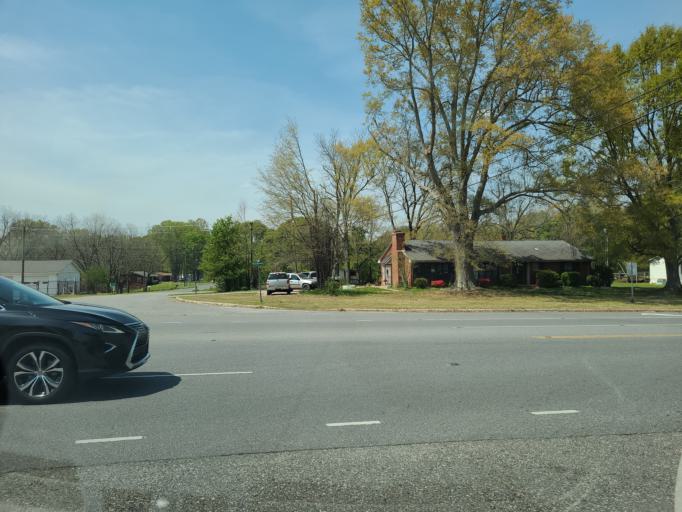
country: US
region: North Carolina
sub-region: Cleveland County
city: Shelby
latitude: 35.2639
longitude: -81.4984
